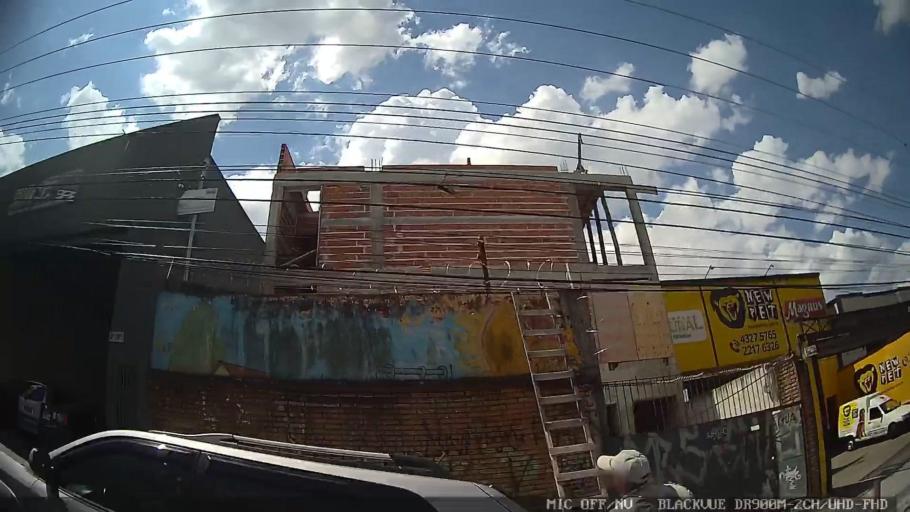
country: BR
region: Sao Paulo
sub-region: Sao Caetano Do Sul
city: Sao Caetano do Sul
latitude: -23.5570
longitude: -46.4723
